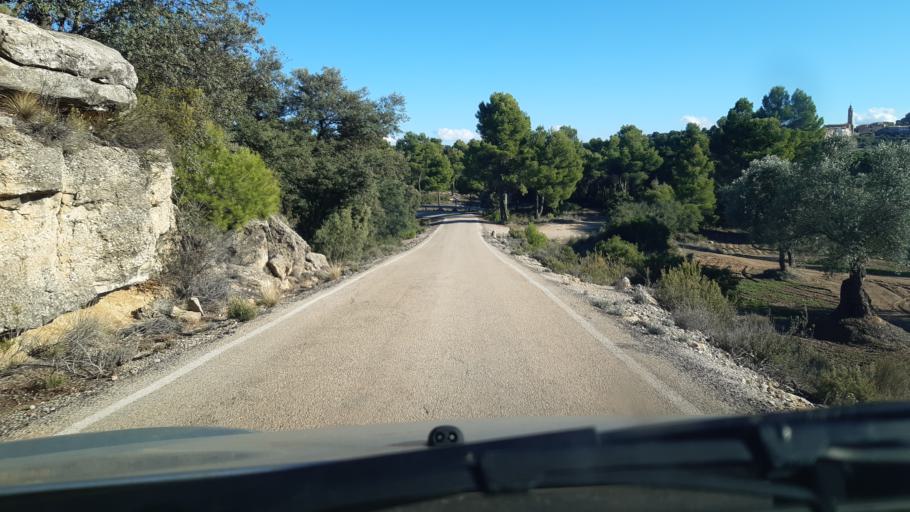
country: ES
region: Aragon
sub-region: Provincia de Teruel
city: Fornoles
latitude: 40.9035
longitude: -0.0097
